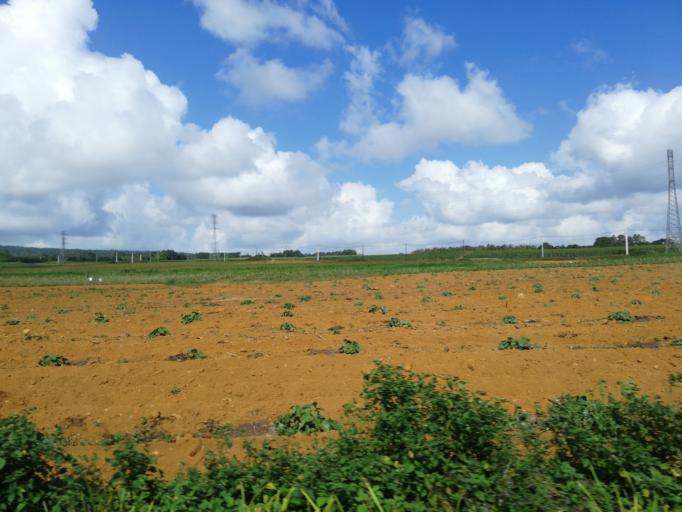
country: MU
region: Pamplemousses
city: Creve Coeur
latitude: -20.2102
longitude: 57.5564
